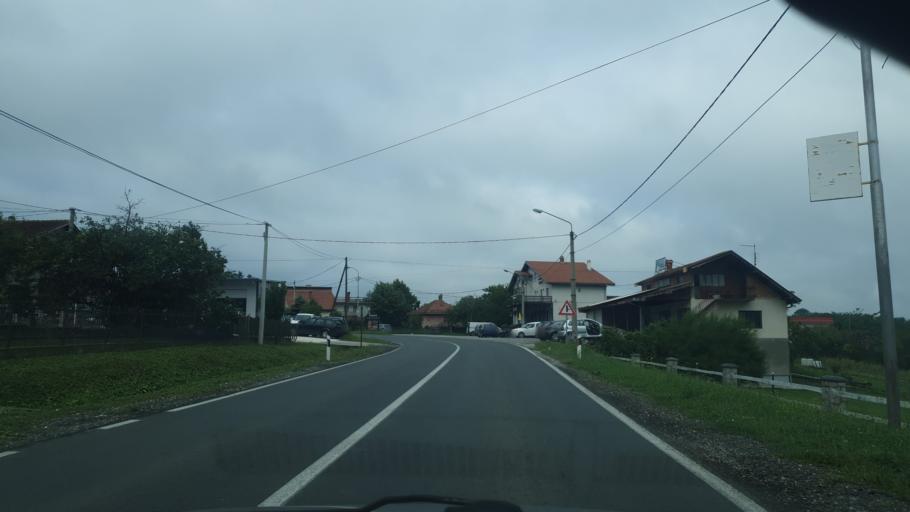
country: RS
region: Central Serbia
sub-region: Sumadijski Okrug
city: Topola
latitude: 44.2656
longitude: 20.6889
